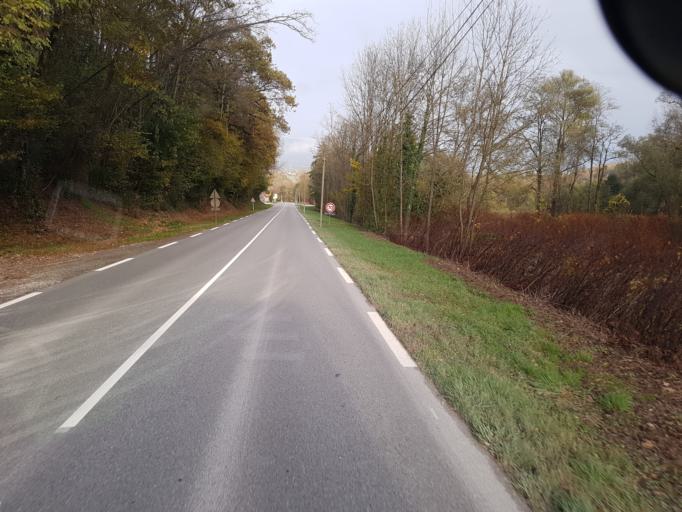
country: FR
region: Rhone-Alpes
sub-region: Departement de la Haute-Savoie
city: Frangy
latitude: 46.0190
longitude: 5.8710
